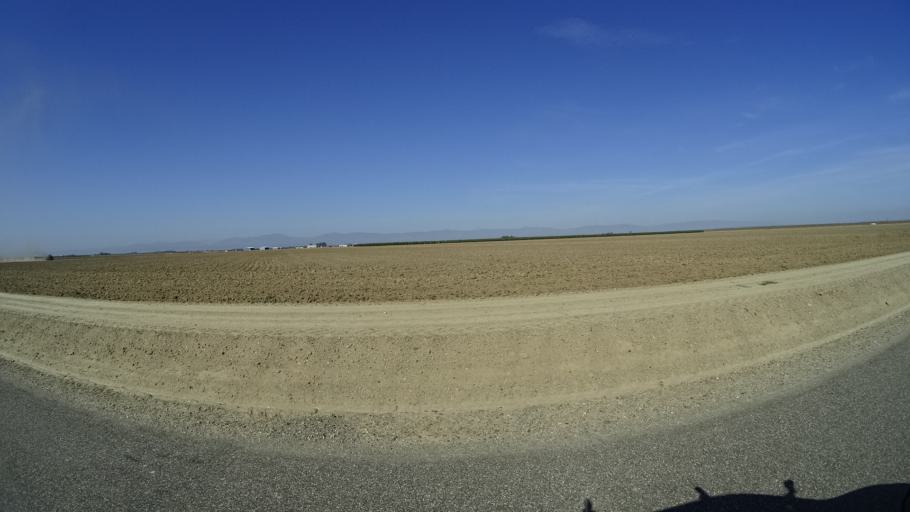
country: US
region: California
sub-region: Glenn County
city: Willows
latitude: 39.6054
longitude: -122.1169
